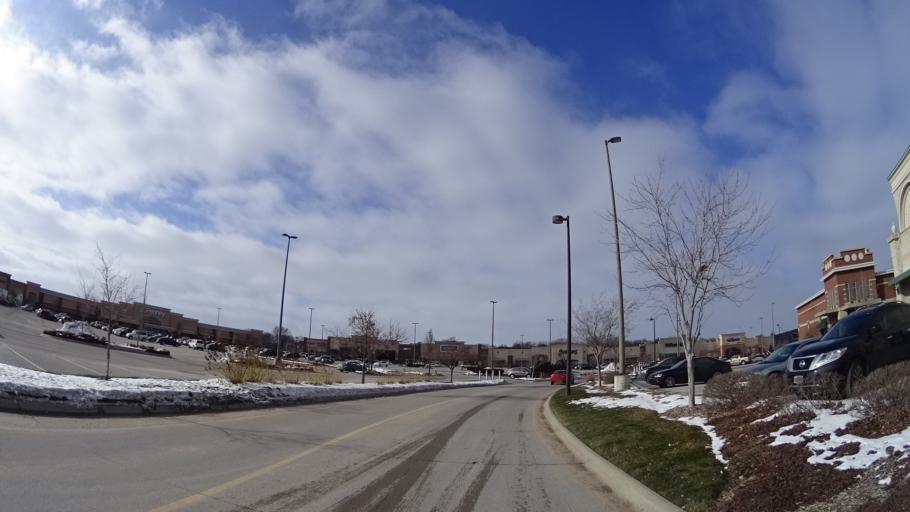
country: US
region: Nebraska
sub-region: Sarpy County
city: Papillion
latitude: 41.1344
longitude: -96.0289
